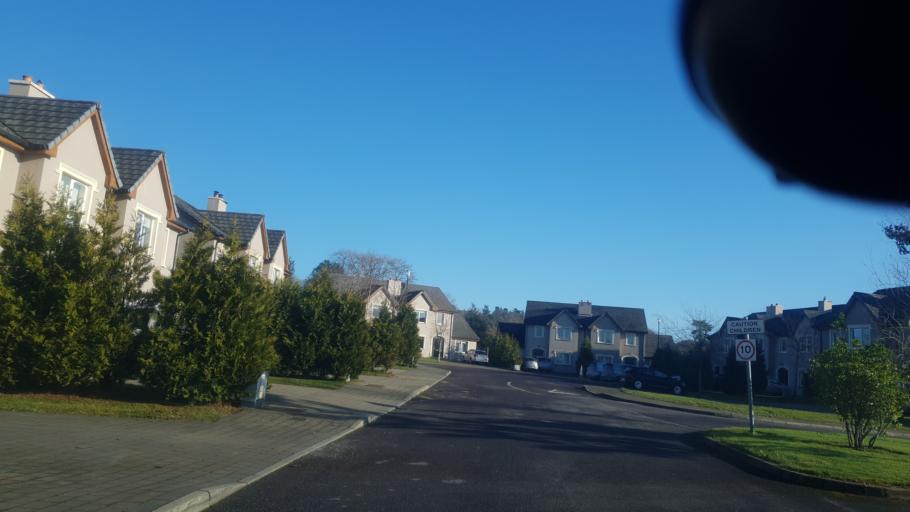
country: IE
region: Munster
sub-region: Ciarrai
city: Cill Airne
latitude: 52.0940
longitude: -9.4753
